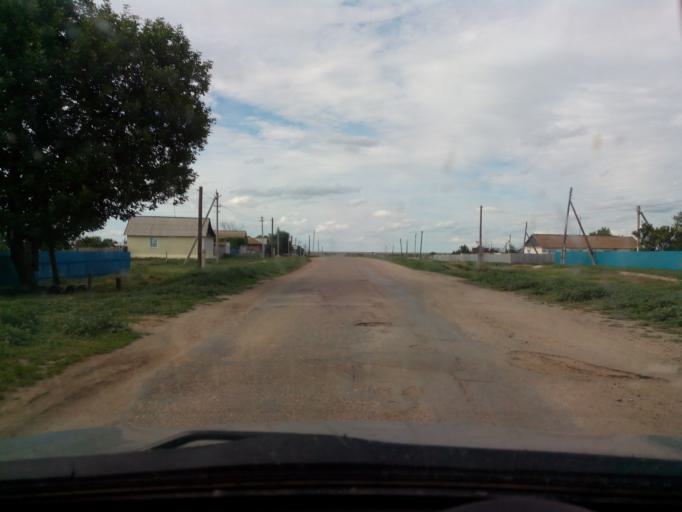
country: RU
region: Volgograd
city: Leninsk
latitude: 48.6683
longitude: 45.3680
